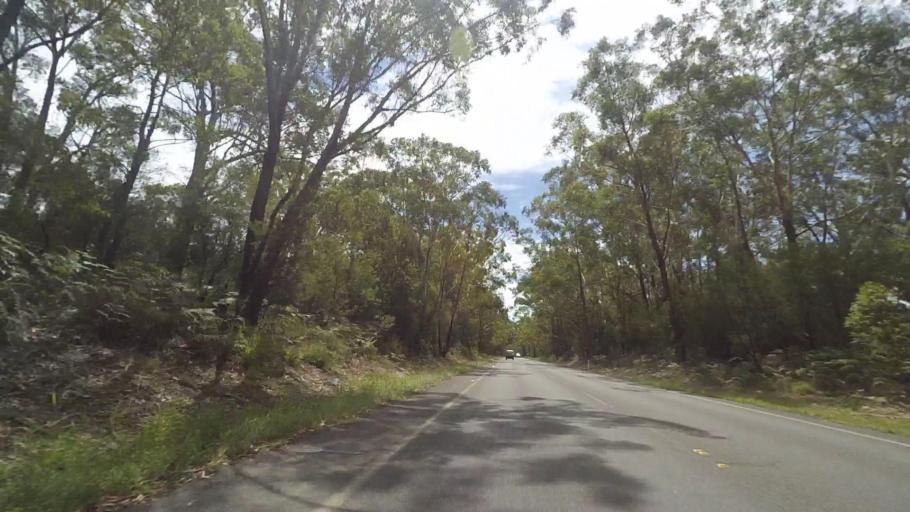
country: AU
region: New South Wales
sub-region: Port Stephens Shire
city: Medowie
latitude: -32.7746
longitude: 151.8709
